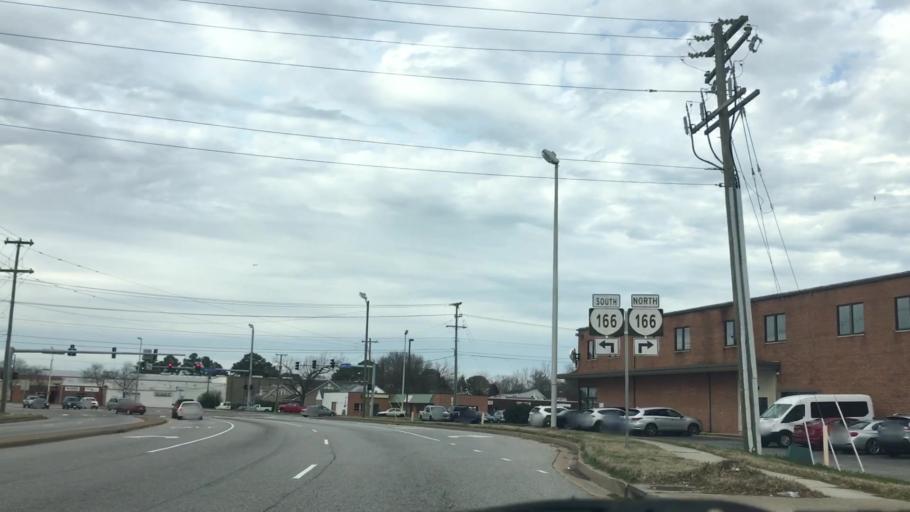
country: US
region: Virginia
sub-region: City of Norfolk
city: Norfolk
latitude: 36.8622
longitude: -76.2436
